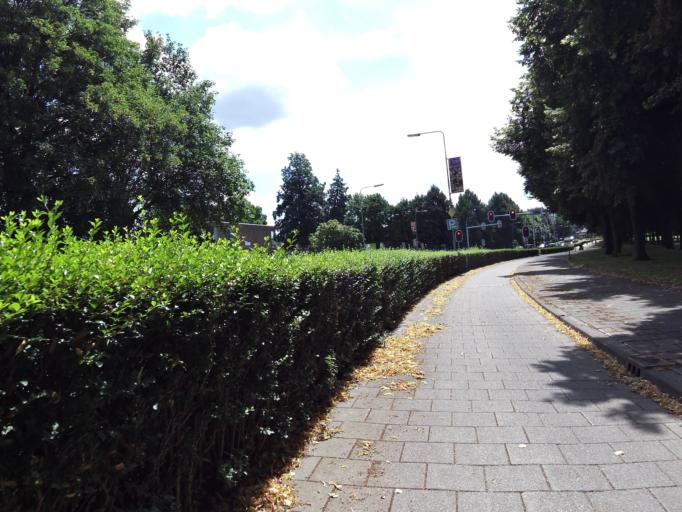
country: NL
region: Limburg
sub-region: Gemeente Sittard-Geleen
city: Sittard
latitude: 50.9986
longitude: 5.8757
